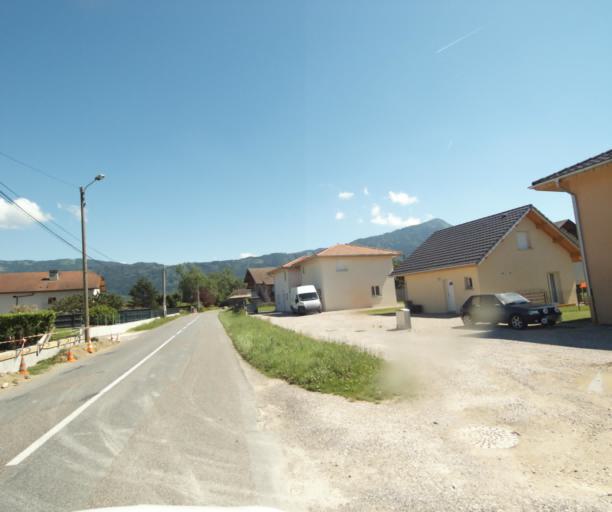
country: FR
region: Rhone-Alpes
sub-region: Departement de la Haute-Savoie
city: Bons-en-Chablais
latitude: 46.2761
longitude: 6.3610
